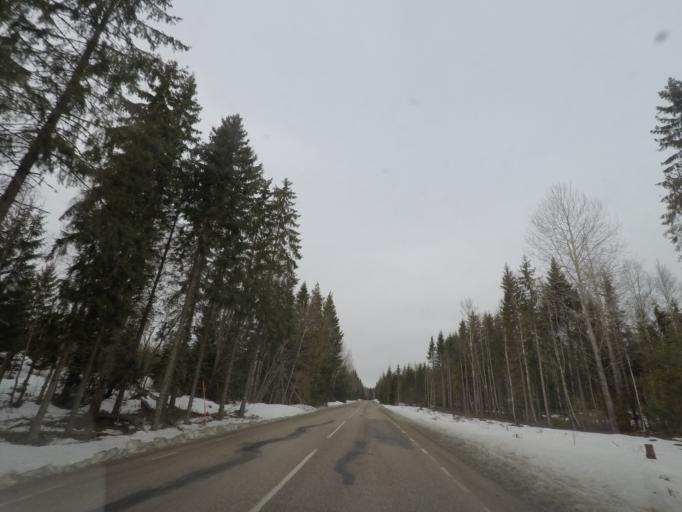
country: SE
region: Vaestmanland
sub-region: Vasteras
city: Skultuna
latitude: 59.7425
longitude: 16.3739
